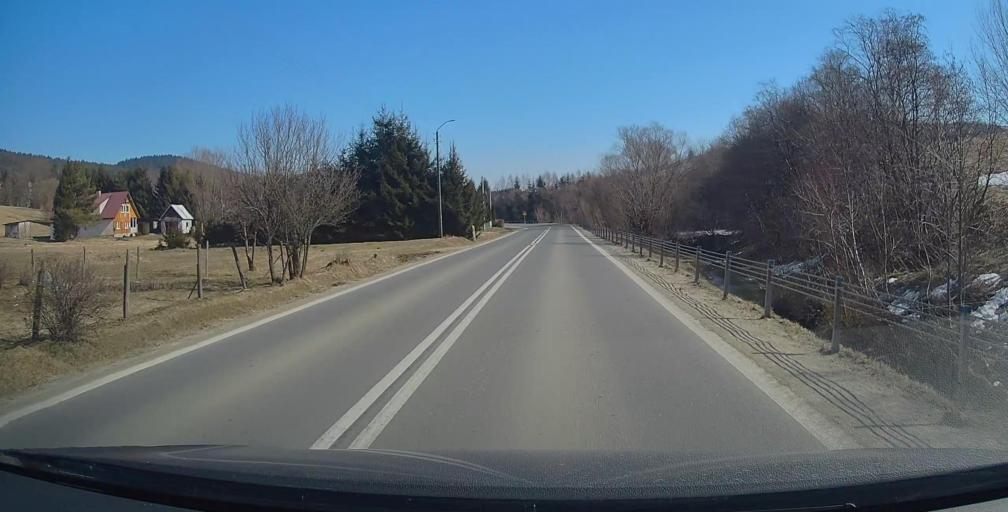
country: PL
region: Subcarpathian Voivodeship
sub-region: Powiat bieszczadzki
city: Ustrzyki Dolne
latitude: 49.4933
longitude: 22.6399
